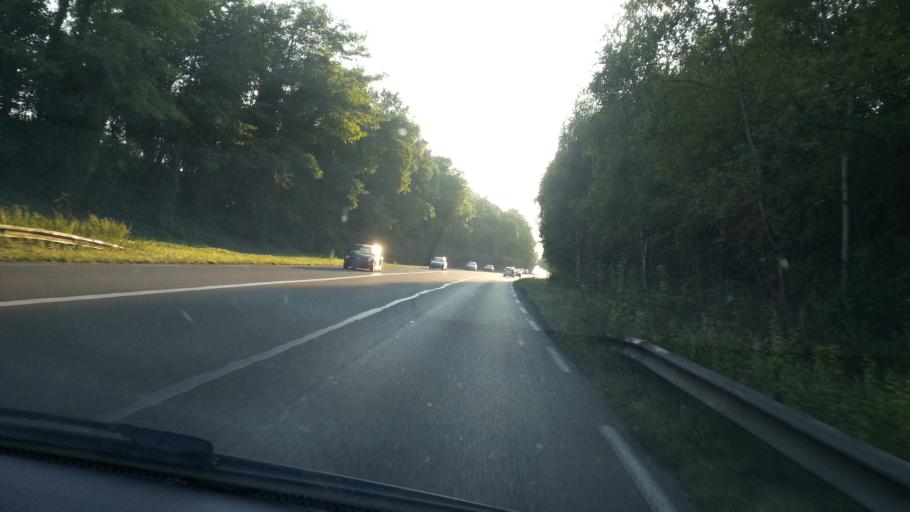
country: FR
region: Picardie
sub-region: Departement de l'Oise
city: Brenouille
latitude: 49.3096
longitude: 2.5451
